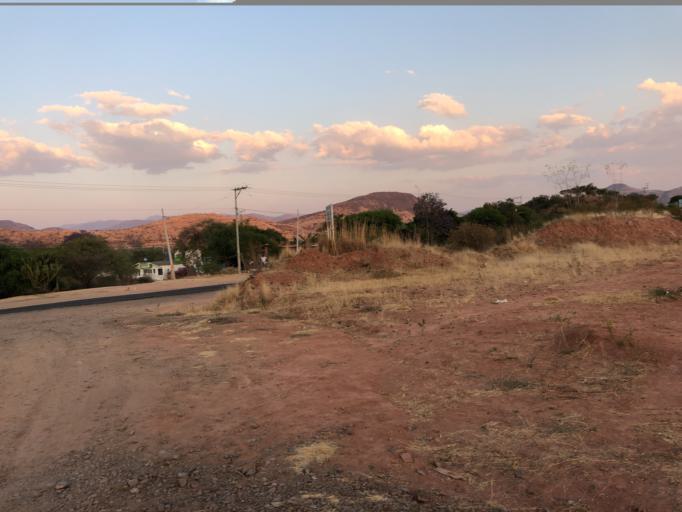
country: MX
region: Oaxaca
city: Ciudad de Huajuapam de Leon
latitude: 17.8369
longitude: -97.7916
